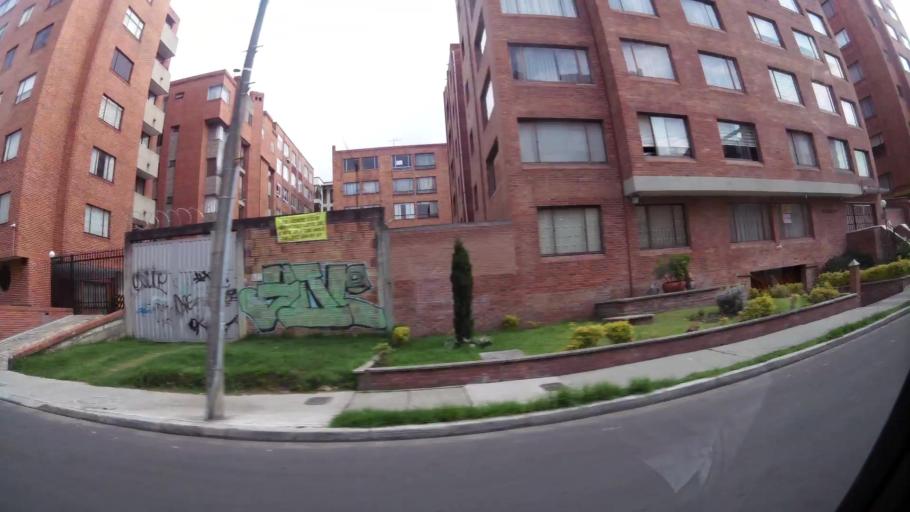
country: CO
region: Bogota D.C.
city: Barrio San Luis
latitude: 4.7336
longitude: -74.0546
